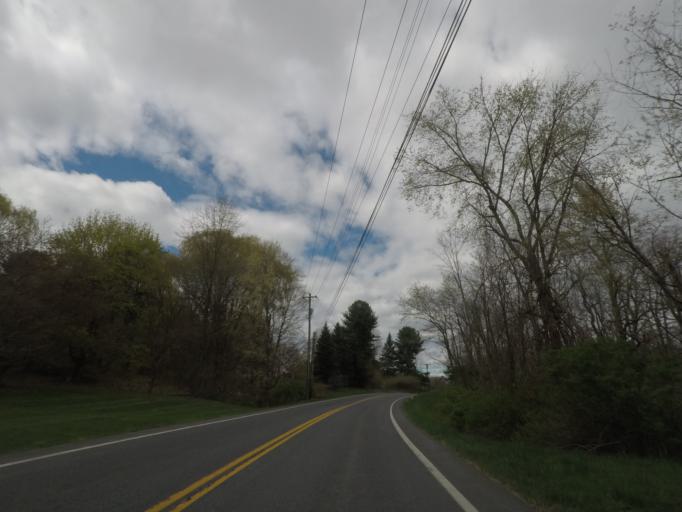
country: US
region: New York
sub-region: Columbia County
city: Philmont
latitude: 42.2628
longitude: -73.6664
